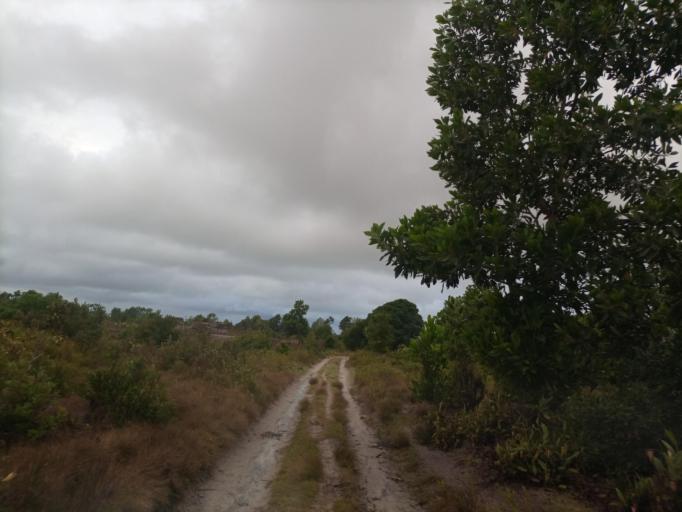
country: MG
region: Anosy
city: Fort Dauphin
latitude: -24.6474
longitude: 47.2077
